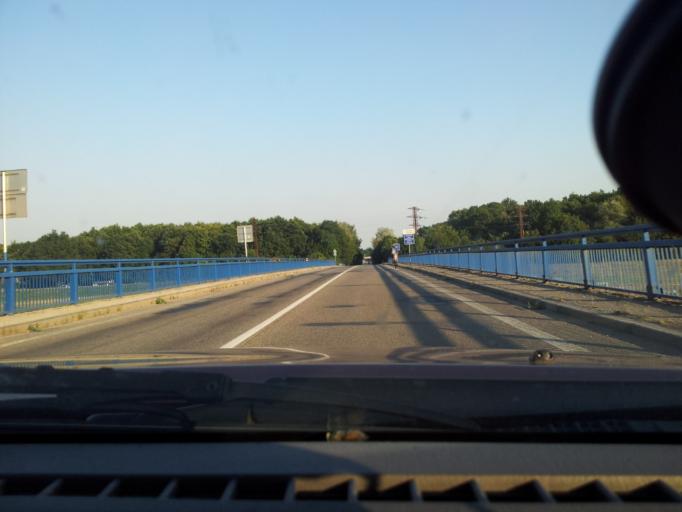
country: CZ
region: South Moravian
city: Hodonin
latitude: 48.8386
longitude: 17.1297
